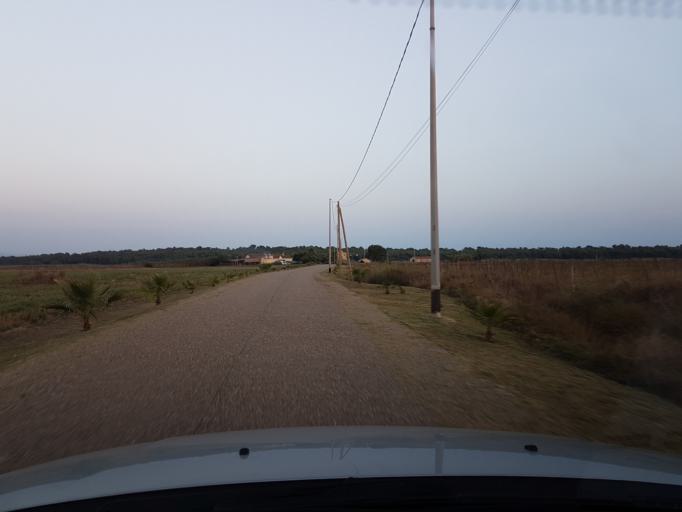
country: IT
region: Sardinia
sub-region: Provincia di Oristano
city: Cabras
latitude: 39.9163
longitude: 8.5081
